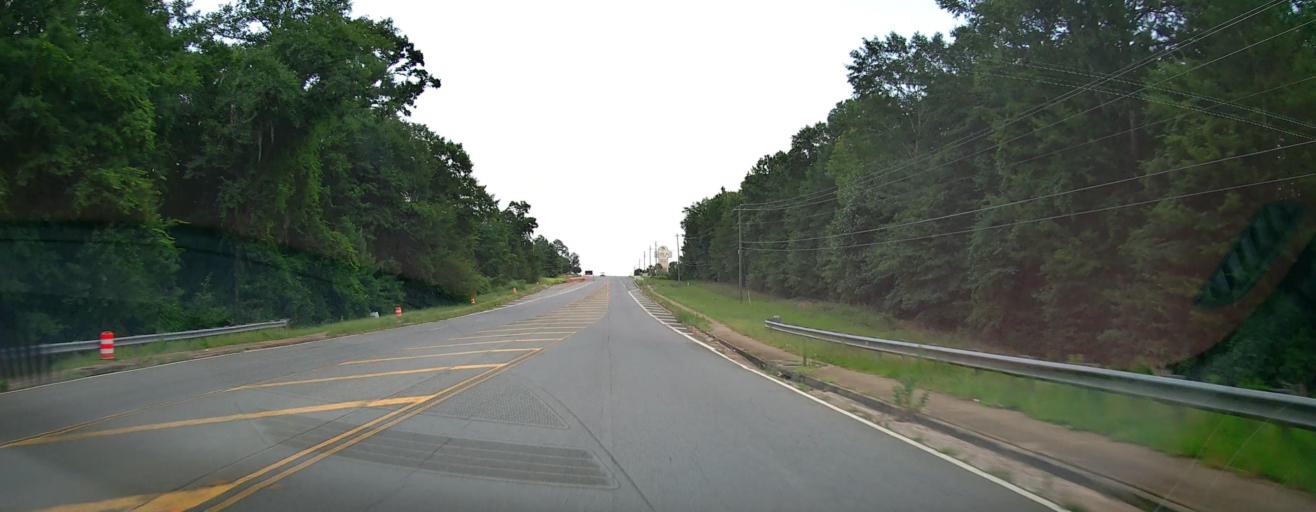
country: US
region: Georgia
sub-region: Laurens County
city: Dublin
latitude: 32.5467
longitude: -82.9346
